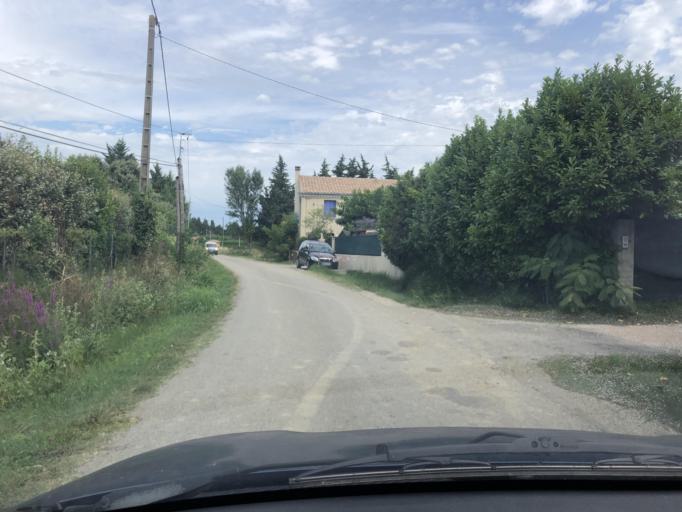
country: FR
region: Provence-Alpes-Cote d'Azur
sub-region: Departement du Vaucluse
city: Piolenc
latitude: 44.1602
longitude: 4.7618
